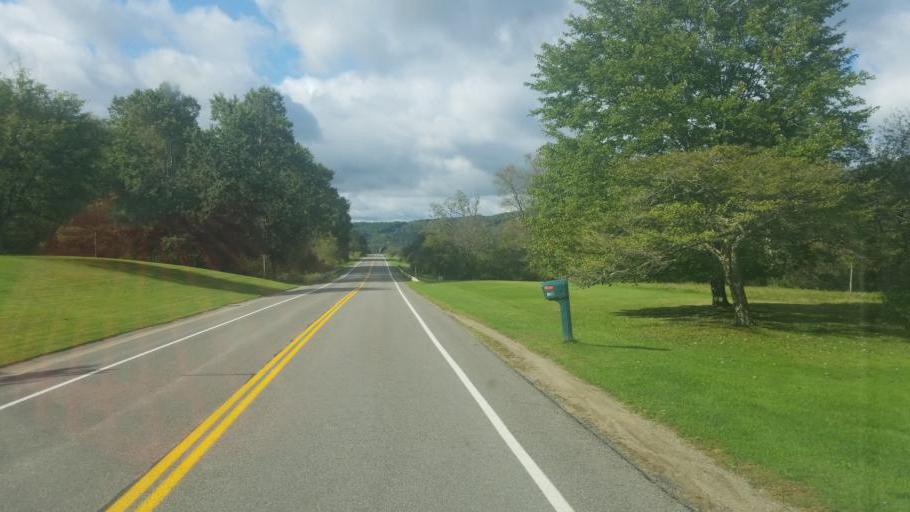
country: US
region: New York
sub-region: Cattaraugus County
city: Weston Mills
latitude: 42.1411
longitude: -78.3269
